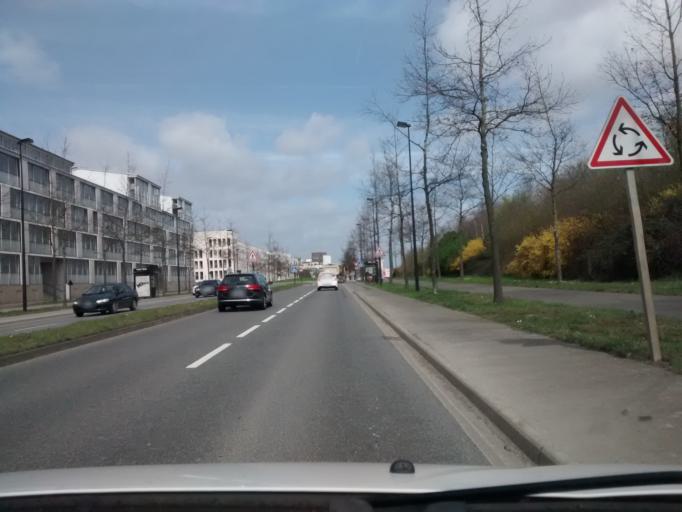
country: FR
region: Brittany
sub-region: Departement d'Ille-et-Vilaine
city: Saint-Jacques-de-la-Lande
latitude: 48.0772
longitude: -1.7124
